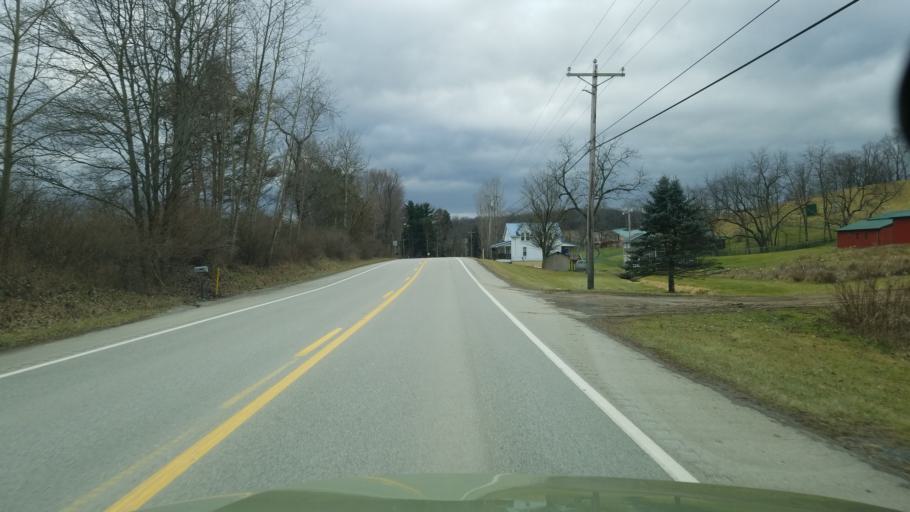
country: US
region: Pennsylvania
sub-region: Indiana County
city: Clymer
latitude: 40.7912
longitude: -79.0543
